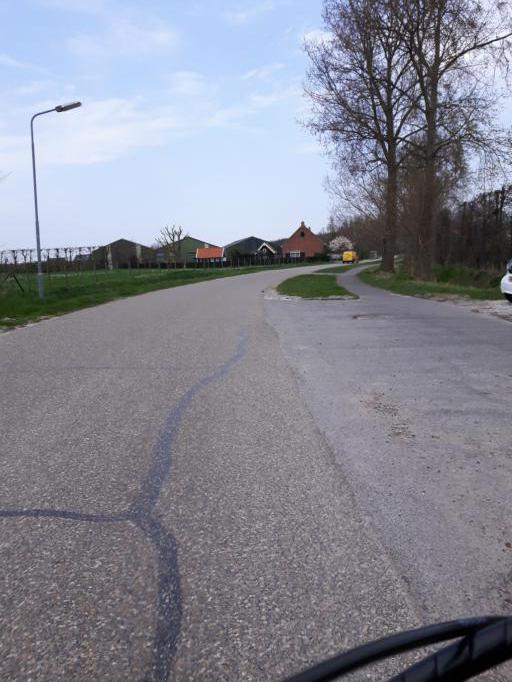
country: NL
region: Zeeland
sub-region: Gemeente Reimerswaal
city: Yerseke
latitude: 51.5182
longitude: 3.9829
